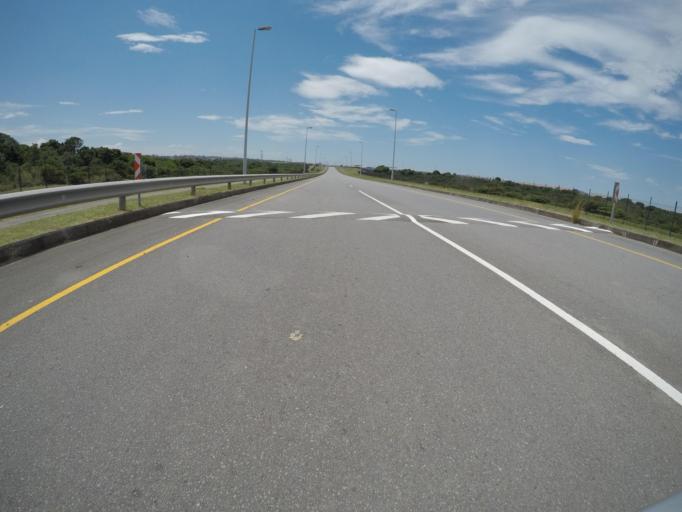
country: ZA
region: Eastern Cape
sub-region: Buffalo City Metropolitan Municipality
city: East London
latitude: -33.0546
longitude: 27.8407
